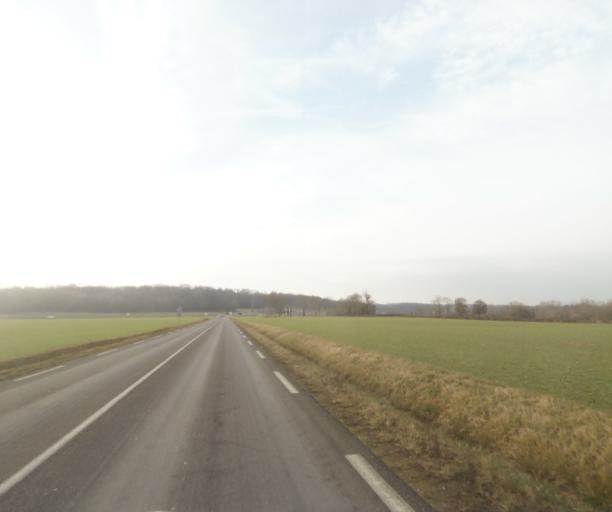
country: FR
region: Champagne-Ardenne
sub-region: Departement de la Haute-Marne
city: Saint-Dizier
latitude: 48.6242
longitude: 4.9301
